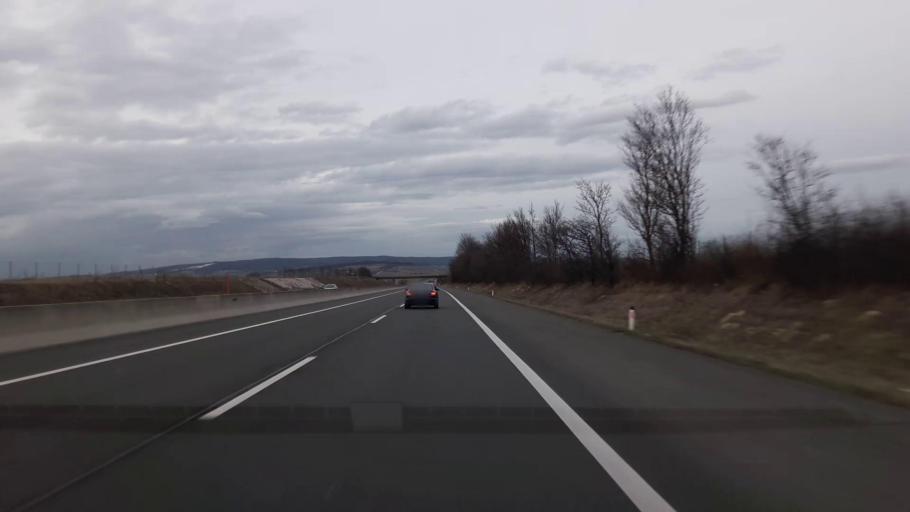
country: AT
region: Burgenland
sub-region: Politischer Bezirk Mattersburg
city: Pottelsdorf
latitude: 47.7721
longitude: 16.4302
